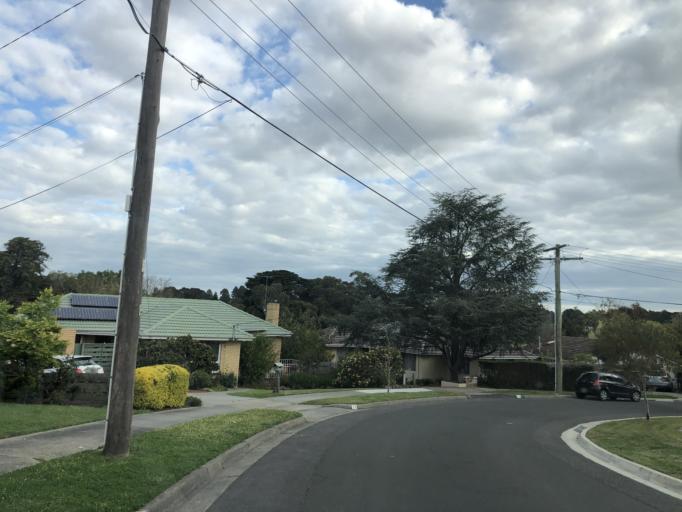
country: AU
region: Victoria
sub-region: Monash
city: Ashwood
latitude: -37.8674
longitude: 145.1176
